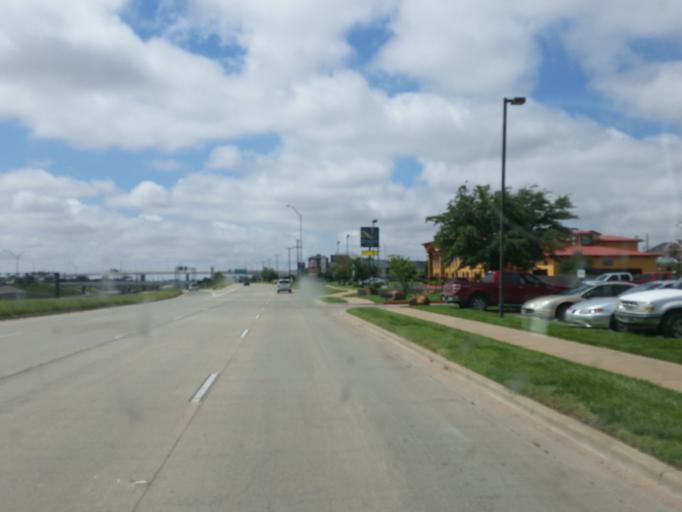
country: US
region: Texas
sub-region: Lubbock County
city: Lubbock
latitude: 33.5430
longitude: -101.8457
